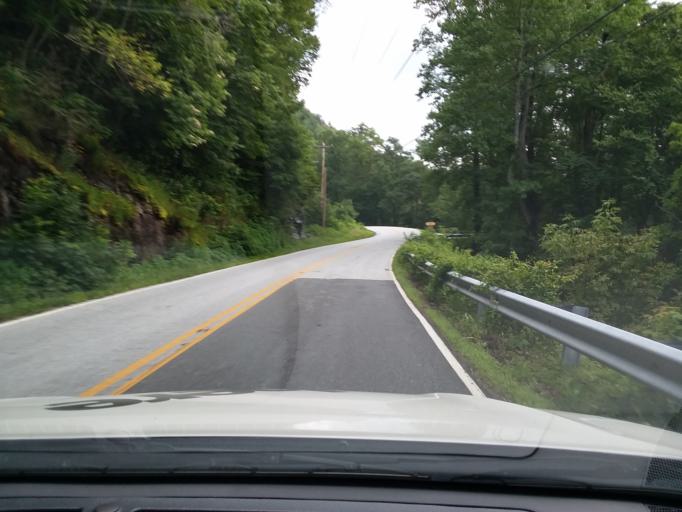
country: US
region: Georgia
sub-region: Rabun County
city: Mountain City
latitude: 35.0303
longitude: -83.2743
